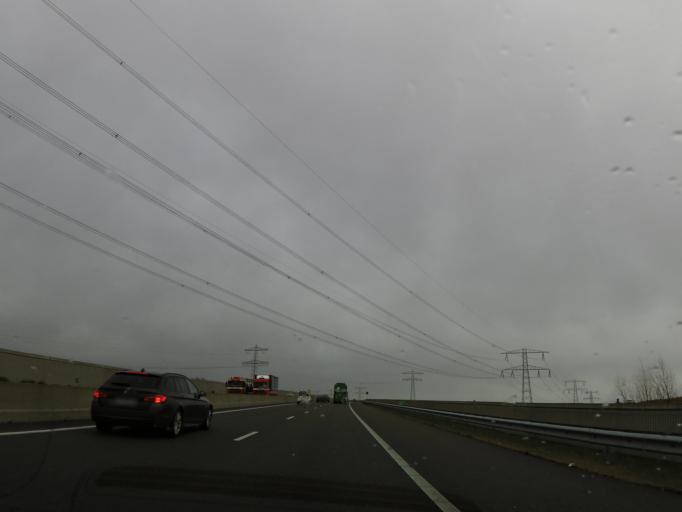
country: NL
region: Limburg
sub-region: Gemeente Roerdalen
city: Montfort
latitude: 51.1444
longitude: 5.9308
